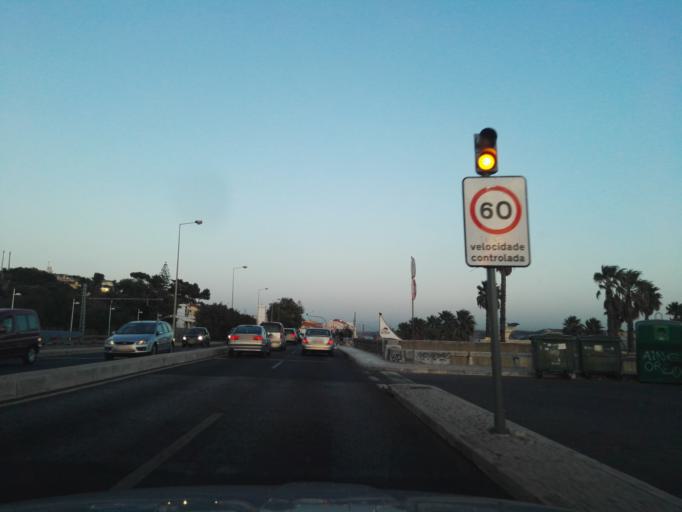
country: PT
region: Lisbon
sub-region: Oeiras
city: Terrugem
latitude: 38.6987
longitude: -9.2764
